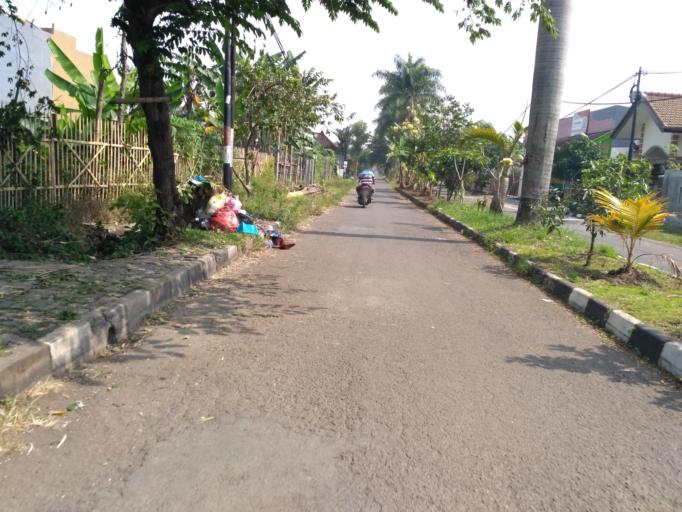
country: ID
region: East Java
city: Malang
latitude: -7.9677
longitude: 112.6713
